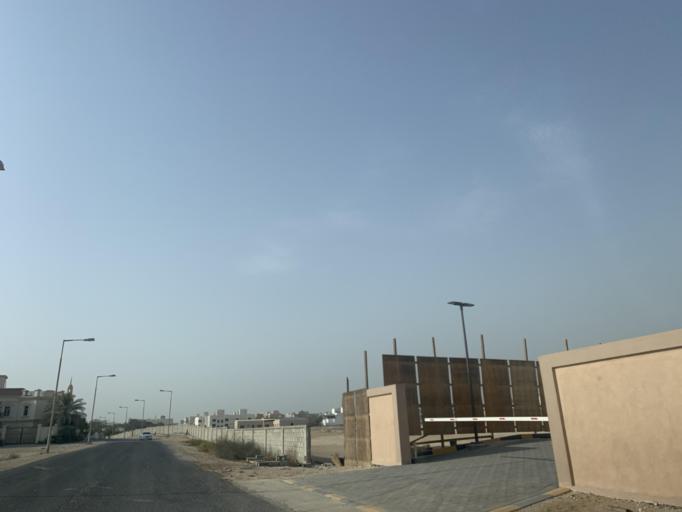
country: BH
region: Central Governorate
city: Madinat Hamad
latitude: 26.1748
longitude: 50.4765
